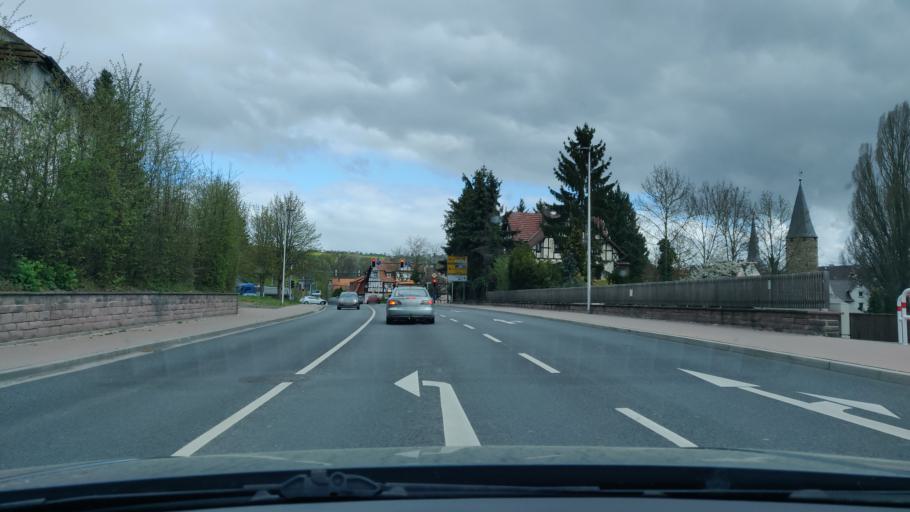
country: DE
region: Hesse
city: Melsungen
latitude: 51.1287
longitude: 9.5415
